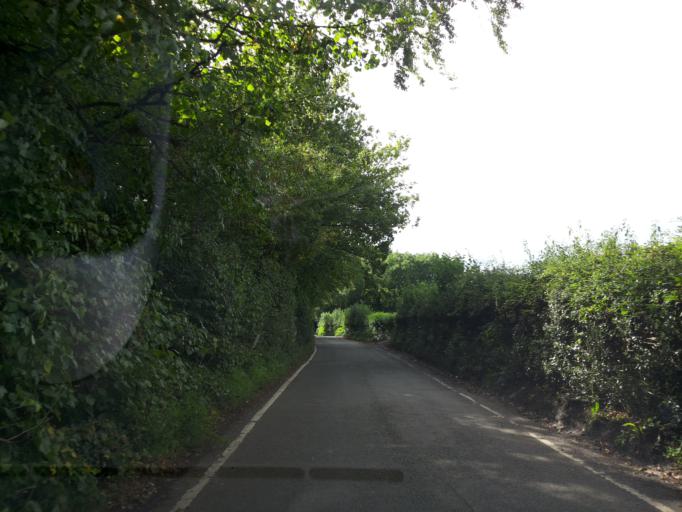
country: GB
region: England
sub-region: Kent
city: Biggin Hill
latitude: 51.3386
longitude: 0.0602
